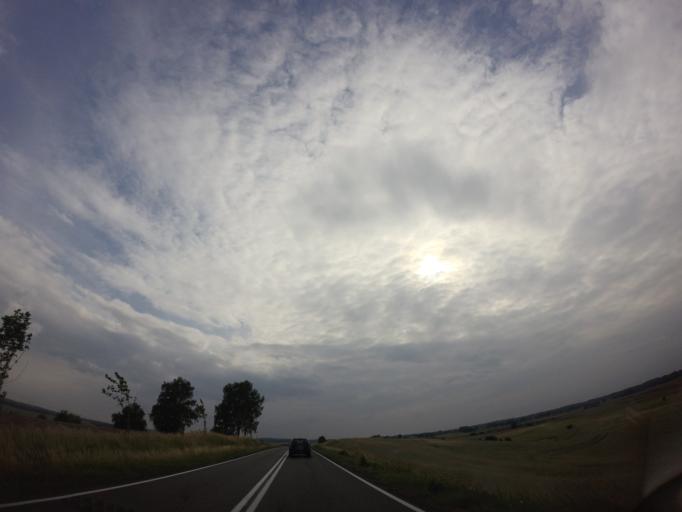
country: PL
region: West Pomeranian Voivodeship
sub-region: Powiat szczecinecki
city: Szczecinek
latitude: 53.6539
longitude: 16.6526
